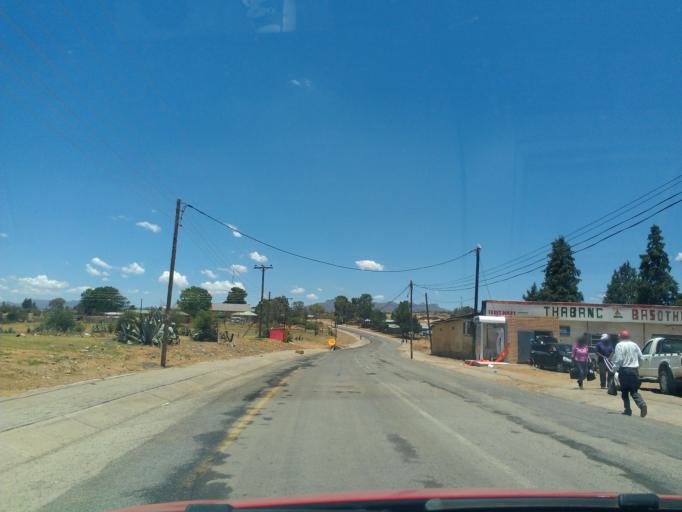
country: LS
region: Berea
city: Teyateyaneng
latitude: -29.1114
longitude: 27.9668
